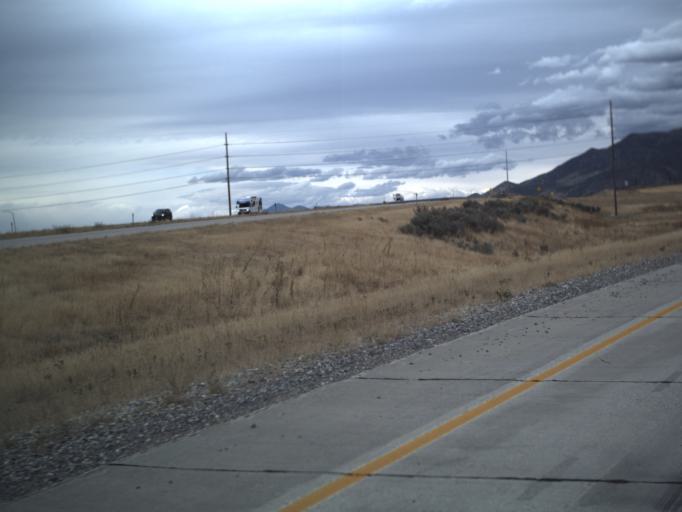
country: US
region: Utah
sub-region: Box Elder County
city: Garland
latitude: 41.8834
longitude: -112.1698
